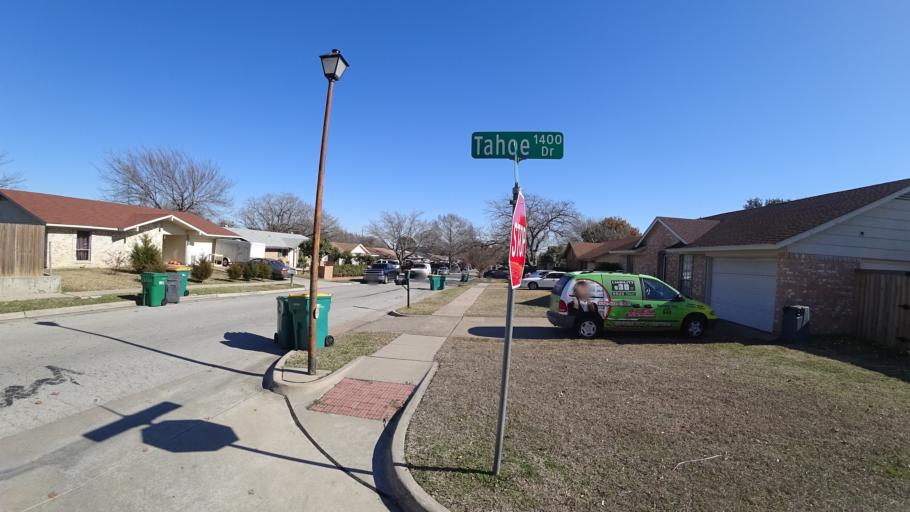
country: US
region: Texas
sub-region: Denton County
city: Lewisville
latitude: 33.0314
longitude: -97.0134
